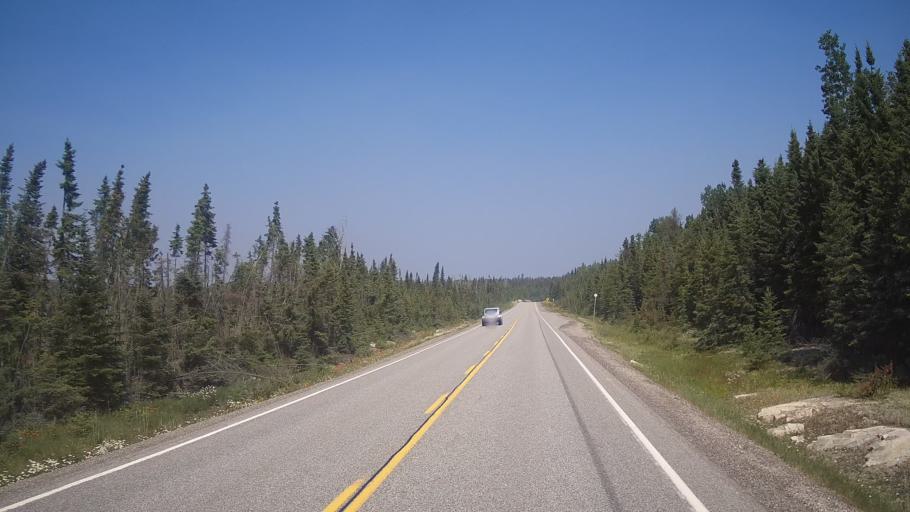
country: CA
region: Ontario
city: Timmins
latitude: 48.0706
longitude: -81.5912
